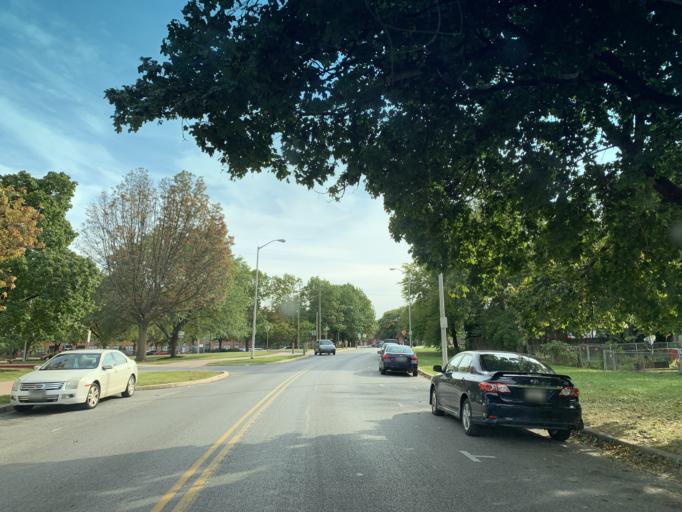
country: US
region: Pennsylvania
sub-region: York County
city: York
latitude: 39.9630
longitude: -76.7183
